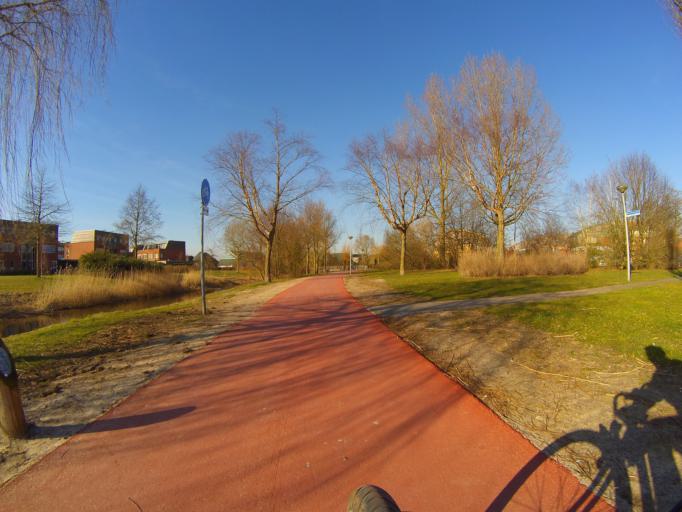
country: NL
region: Gelderland
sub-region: Gemeente Nijkerk
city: Nijkerk
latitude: 52.2167
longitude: 5.4632
